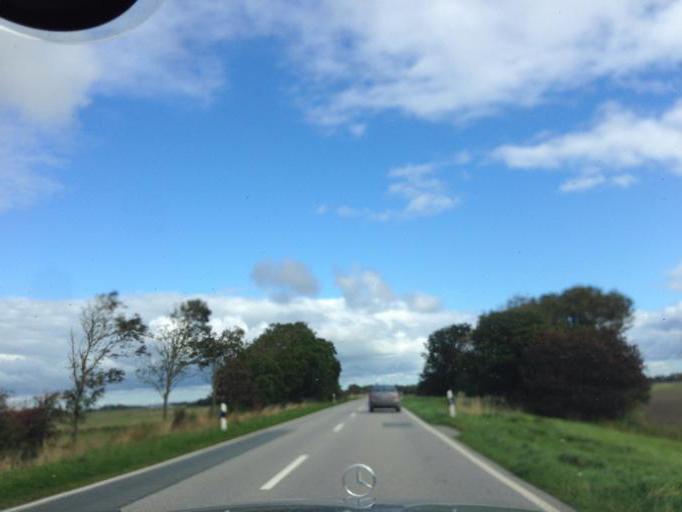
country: DE
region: Schleswig-Holstein
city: Galmsbull
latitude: 54.7739
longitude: 8.7567
